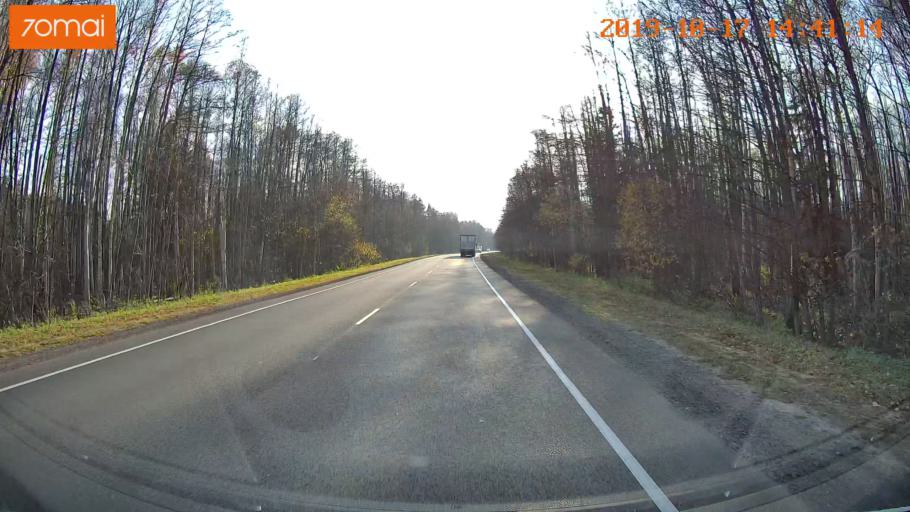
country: RU
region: Rjazan
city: Solotcha
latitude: 54.8475
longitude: 39.9420
